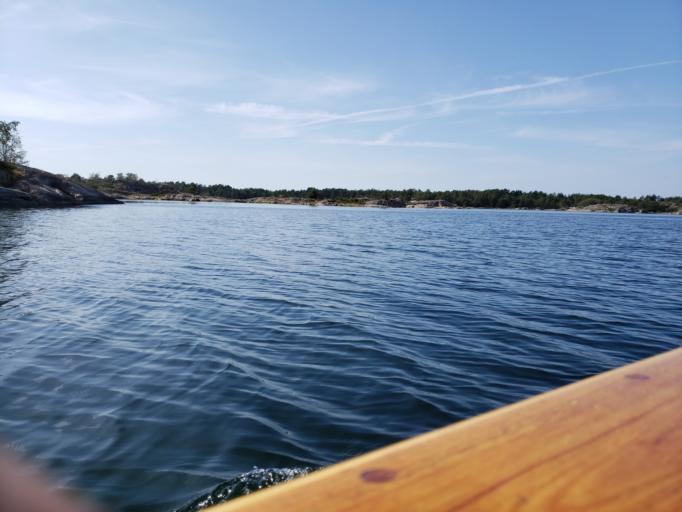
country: FI
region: Varsinais-Suomi
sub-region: Aboland-Turunmaa
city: Dragsfjaerd
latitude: 59.8530
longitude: 22.2129
